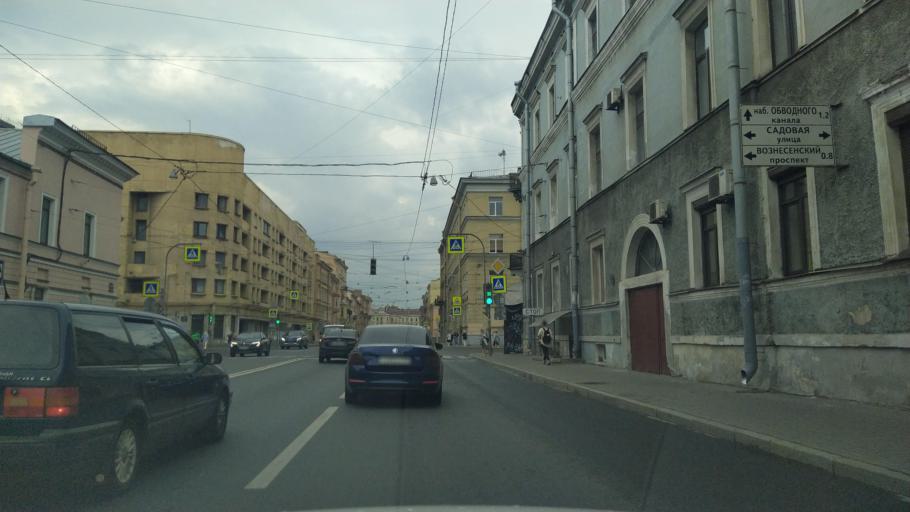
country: RU
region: St.-Petersburg
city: Admiralteisky
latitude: 59.9202
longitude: 30.2946
